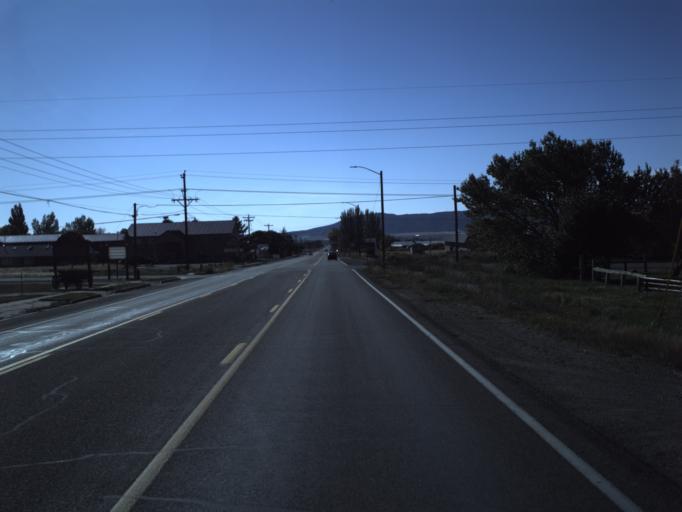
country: US
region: Utah
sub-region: Iron County
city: Parowan
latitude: 37.8388
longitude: -112.8388
